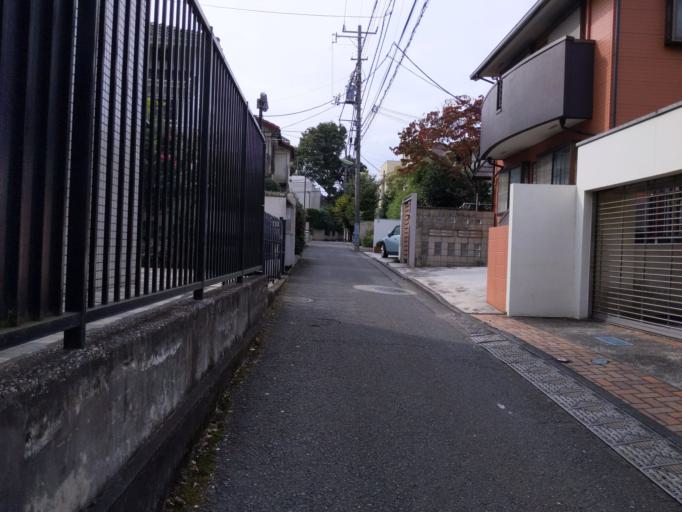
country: JP
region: Tokyo
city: Tokyo
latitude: 35.6580
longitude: 139.6664
